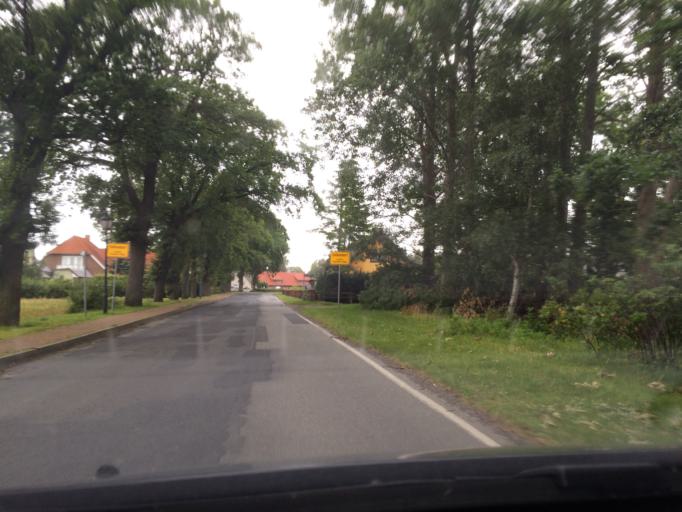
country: DE
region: Mecklenburg-Vorpommern
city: Prohn
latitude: 54.4103
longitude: 13.0151
